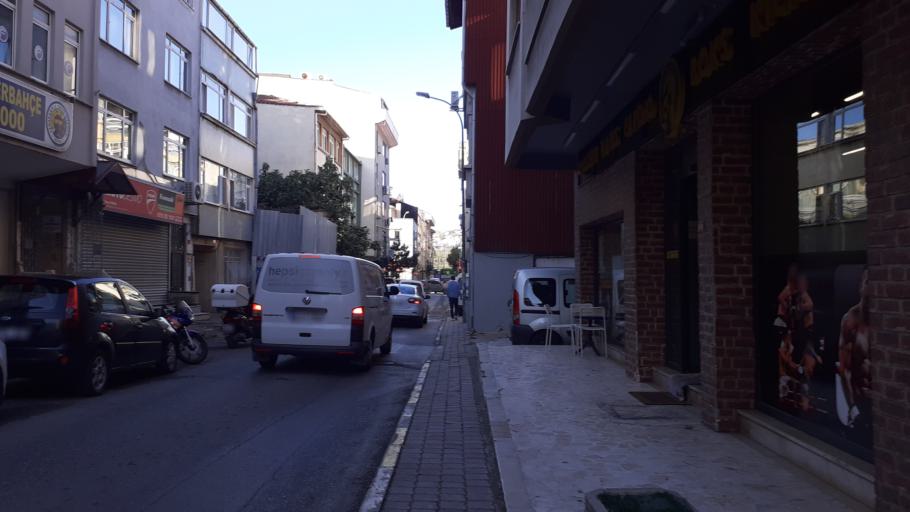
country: TR
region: Istanbul
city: UEskuedar
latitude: 40.9858
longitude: 29.0385
